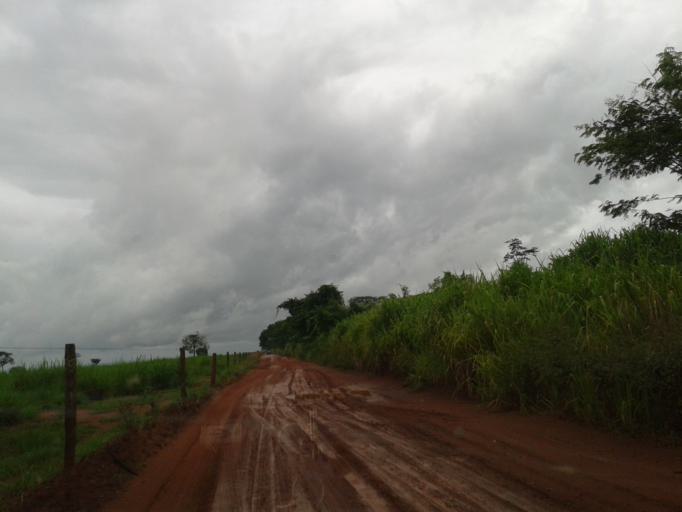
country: BR
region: Minas Gerais
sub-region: Santa Vitoria
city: Santa Vitoria
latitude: -18.7237
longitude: -49.9677
